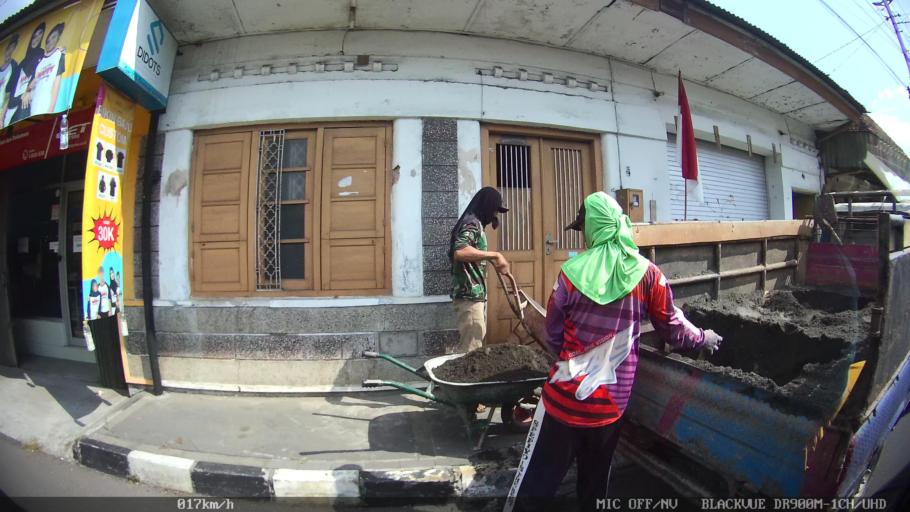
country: ID
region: Daerah Istimewa Yogyakarta
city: Yogyakarta
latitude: -7.8274
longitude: 110.3970
